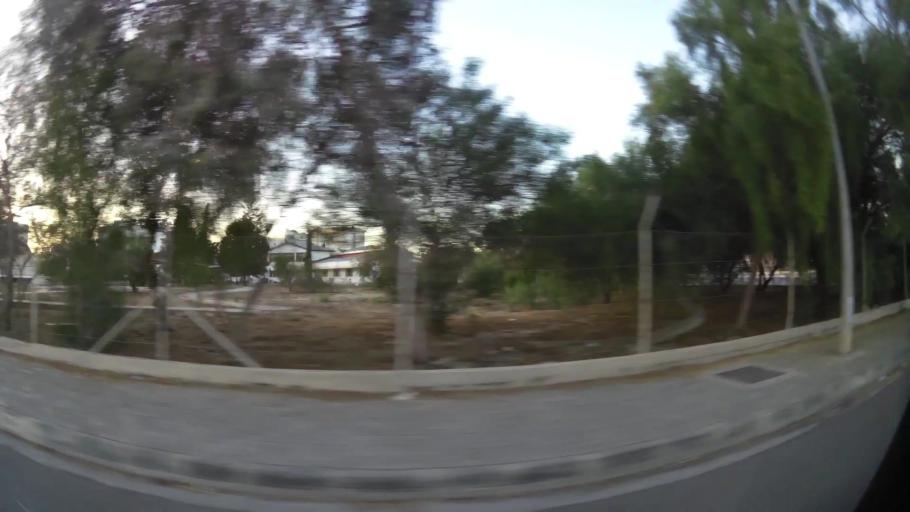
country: CY
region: Lefkosia
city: Nicosia
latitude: 35.2055
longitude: 33.3333
